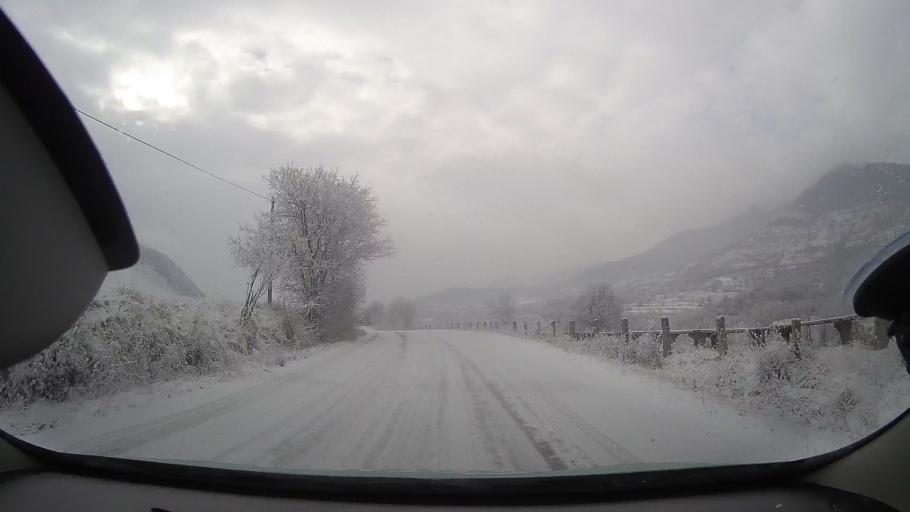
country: RO
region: Alba
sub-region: Comuna Rimetea
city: Rimetea
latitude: 46.4637
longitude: 23.5730
